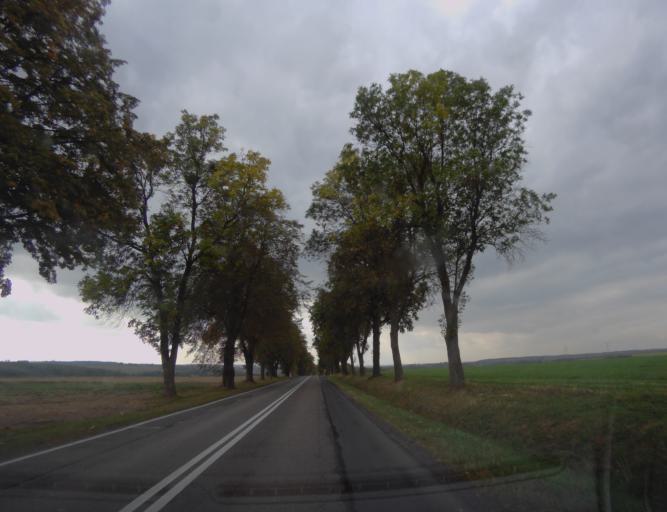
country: PL
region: Lublin Voivodeship
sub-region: Powiat krasnostawski
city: Zolkiewka
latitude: 50.9214
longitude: 22.8784
